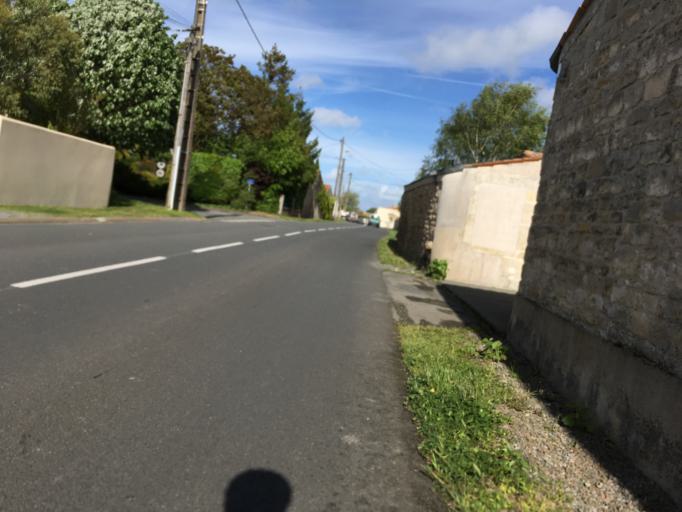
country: FR
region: Poitou-Charentes
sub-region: Departement de la Charente-Maritime
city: Dompierre-sur-Mer
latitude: 46.1788
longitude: -1.0520
